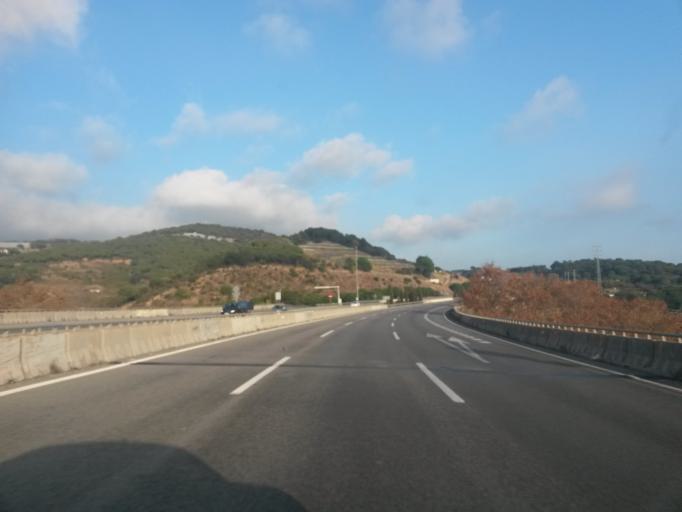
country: ES
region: Catalonia
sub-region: Provincia de Barcelona
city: Sant Pol de Mar
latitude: 41.6051
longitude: 2.6067
